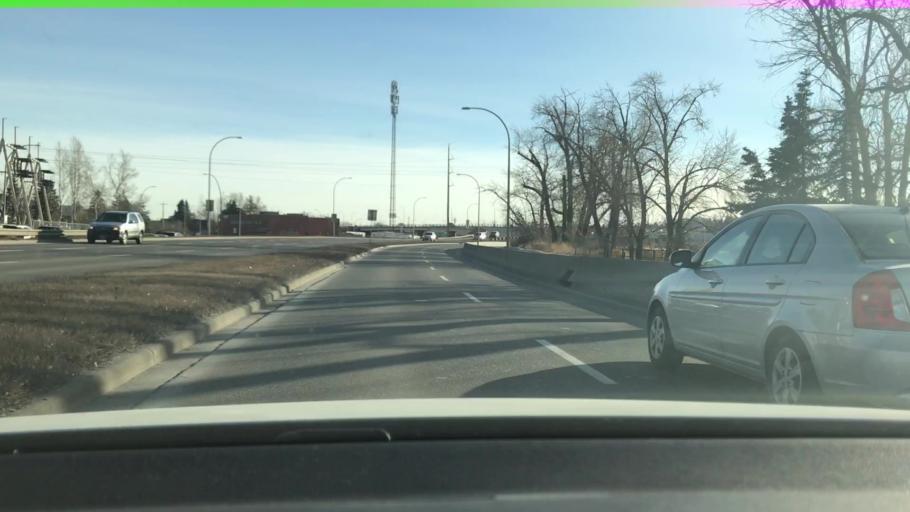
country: CA
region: Alberta
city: Calgary
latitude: 51.0519
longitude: -114.1206
